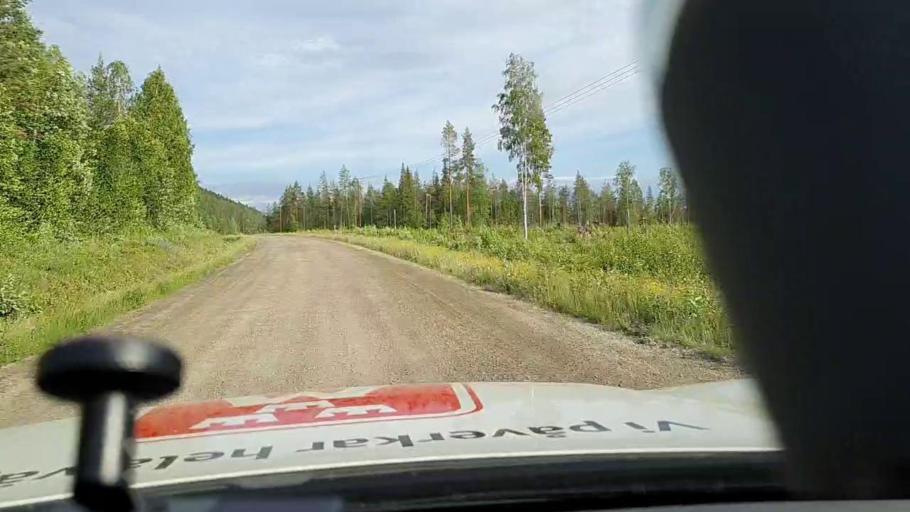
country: SE
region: Norrbotten
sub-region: Alvsbyns Kommun
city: AElvsbyn
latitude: 66.1821
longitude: 21.2203
